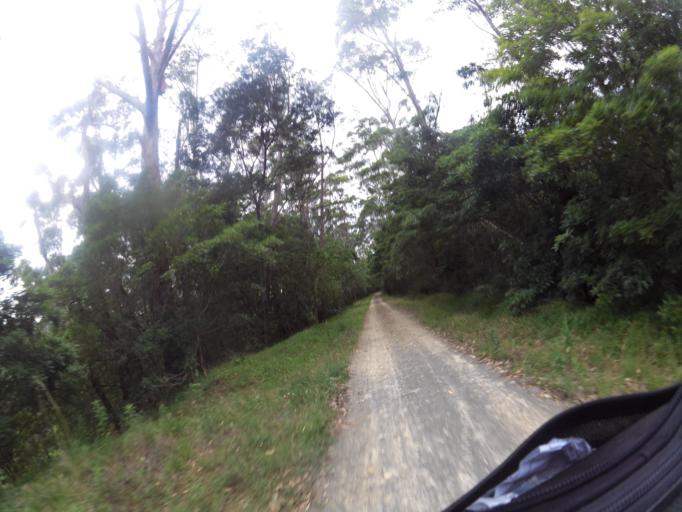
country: AU
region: Victoria
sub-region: East Gippsland
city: Lakes Entrance
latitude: -37.7263
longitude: 148.4274
